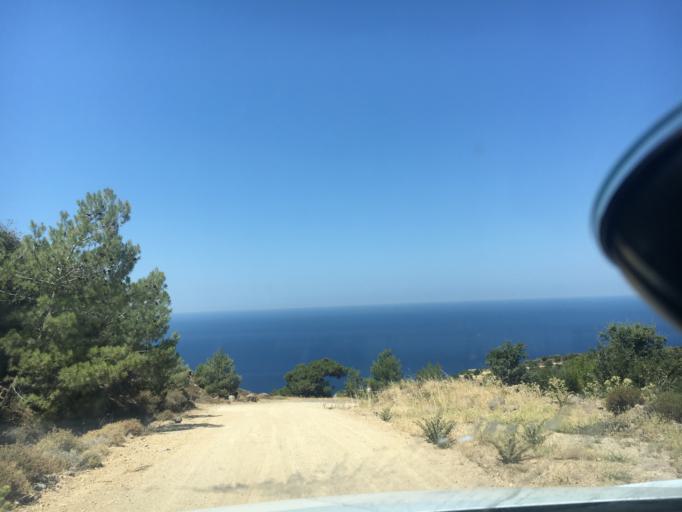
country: TR
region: Canakkale
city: Gulpinar
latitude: 39.4812
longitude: 26.0737
